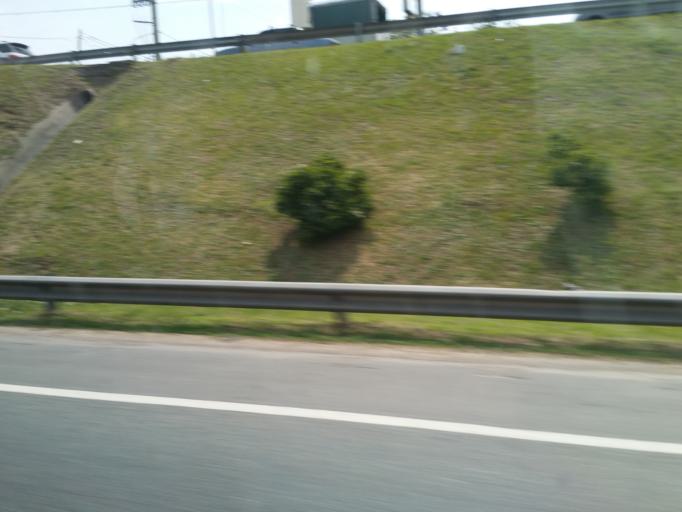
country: AR
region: Buenos Aires F.D.
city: Villa Lugano
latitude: -34.6943
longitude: -58.4918
